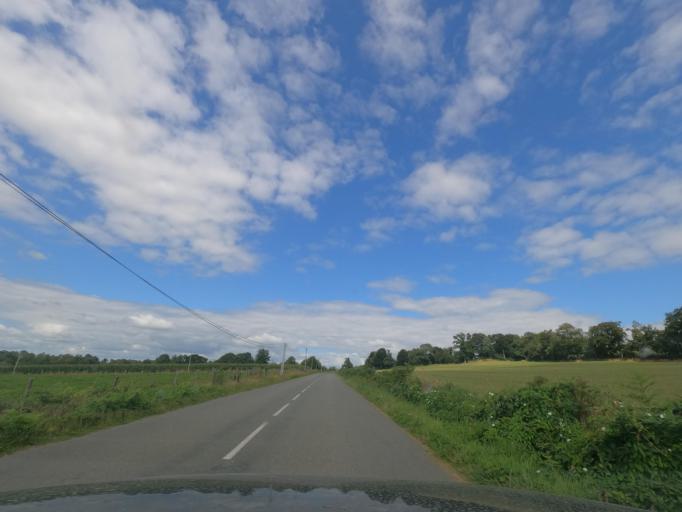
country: FR
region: Pays de la Loire
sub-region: Departement de la Mayenne
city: Landivy
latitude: 48.4678
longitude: -1.0469
